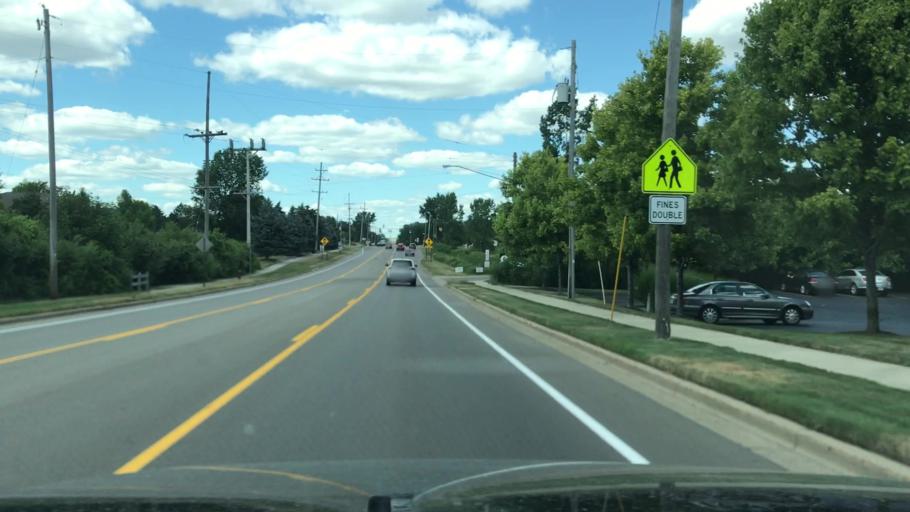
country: US
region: Michigan
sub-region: Kent County
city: Byron Center
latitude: 42.8244
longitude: -85.7230
